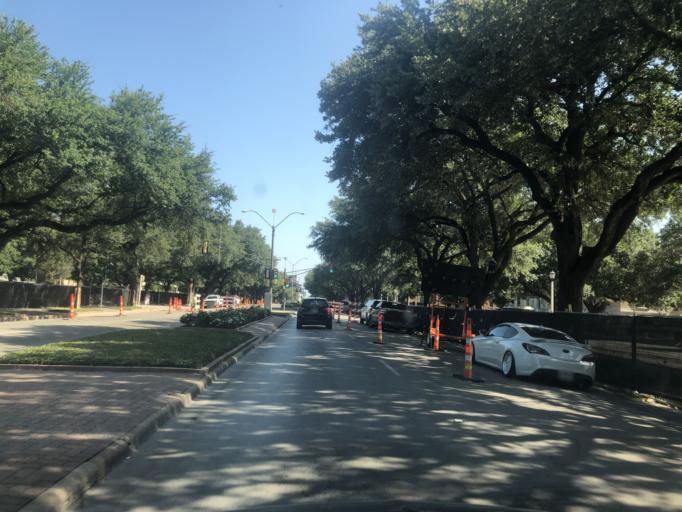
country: US
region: Texas
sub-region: Tarrant County
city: Fort Worth
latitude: 32.7082
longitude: -97.3604
